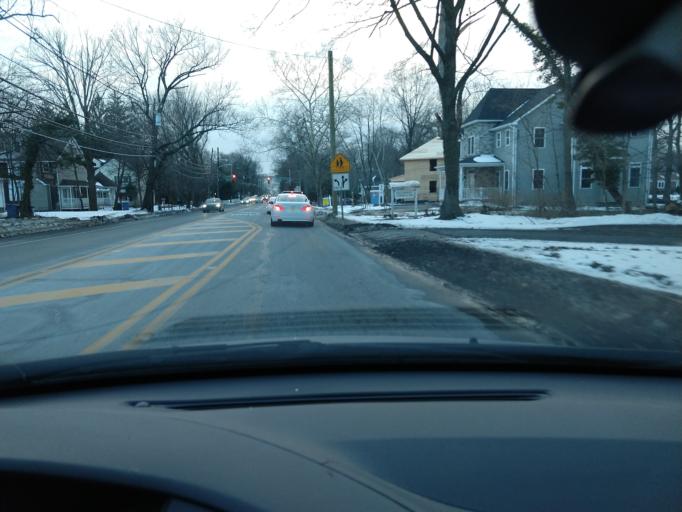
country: US
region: New Jersey
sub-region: Middlesex County
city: Metuchen
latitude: 40.5500
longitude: -74.3537
